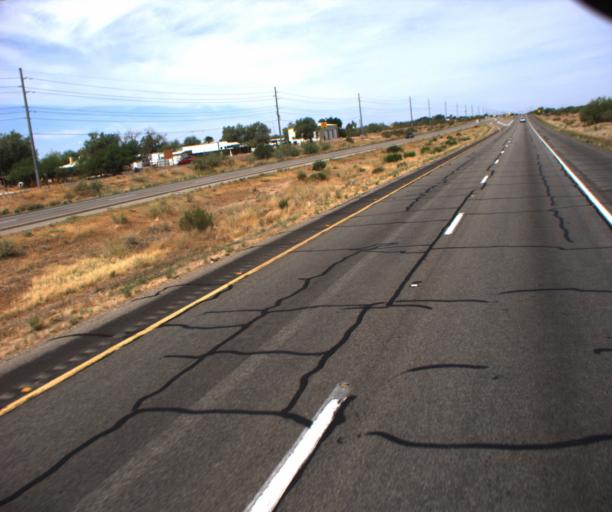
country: US
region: Arizona
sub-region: Maricopa County
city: Sun City West
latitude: 33.7701
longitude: -112.5184
